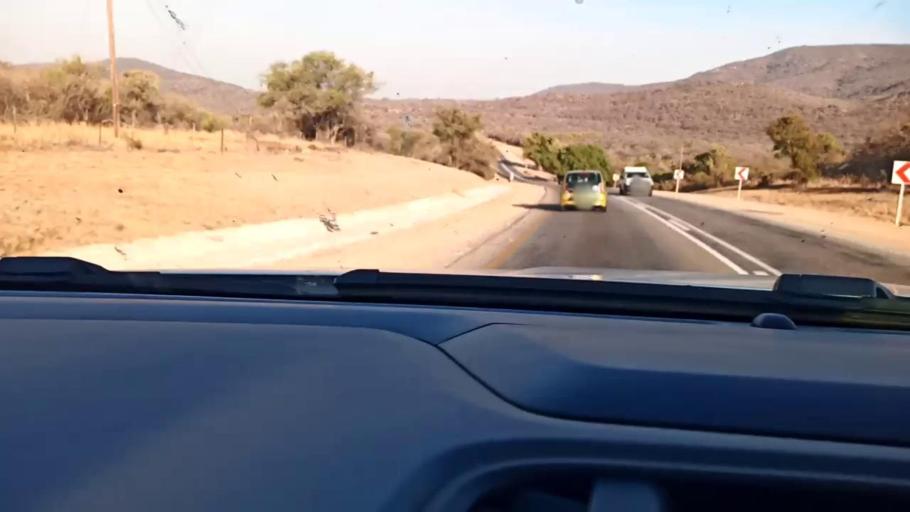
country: ZA
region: Limpopo
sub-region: Mopani District Municipality
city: Duiwelskloof
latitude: -23.6286
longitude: 30.1316
